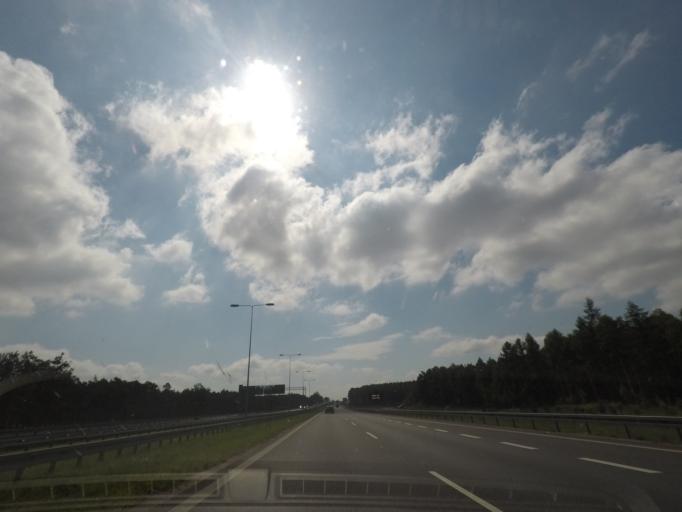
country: PL
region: Kujawsko-Pomorskie
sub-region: Powiat aleksandrowski
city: Ciechocinek
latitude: 52.8633
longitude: 18.7642
